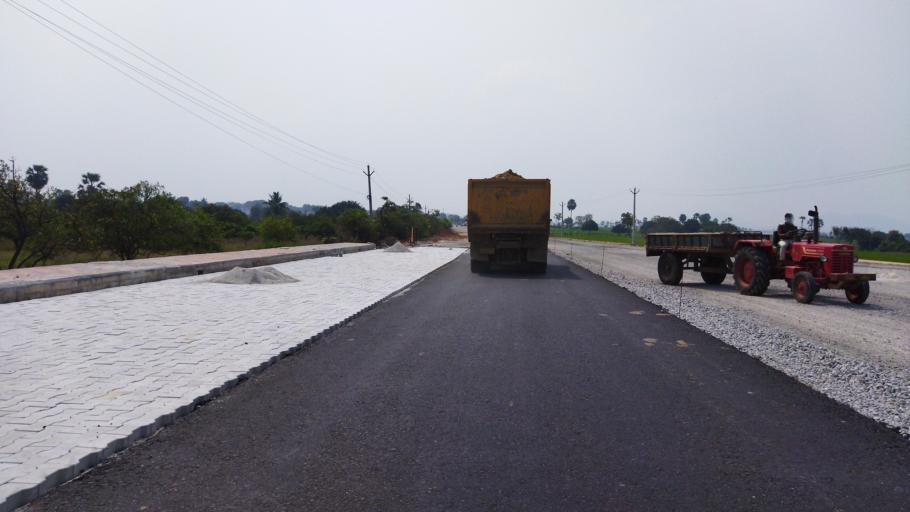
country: IN
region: Telangana
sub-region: Nalgonda
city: Nalgonda
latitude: 17.0889
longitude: 79.3276
